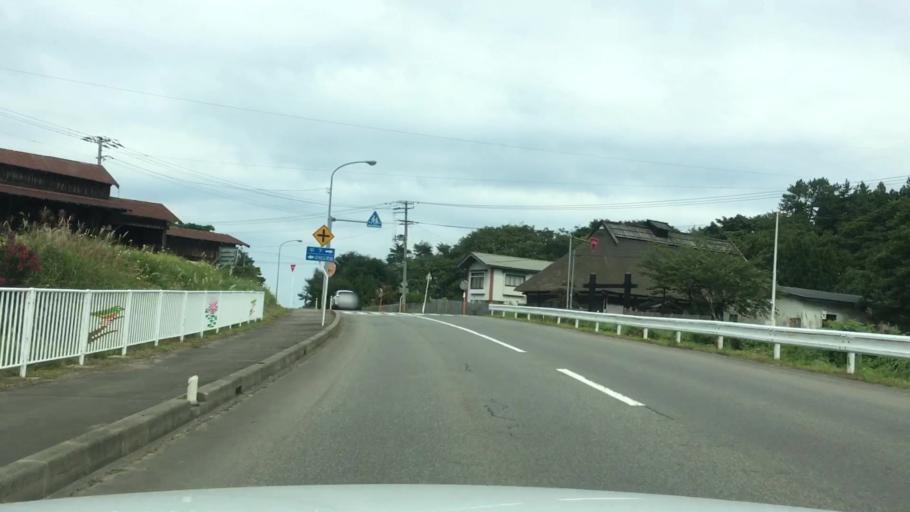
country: JP
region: Aomori
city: Shimokizukuri
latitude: 40.7573
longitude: 140.2306
